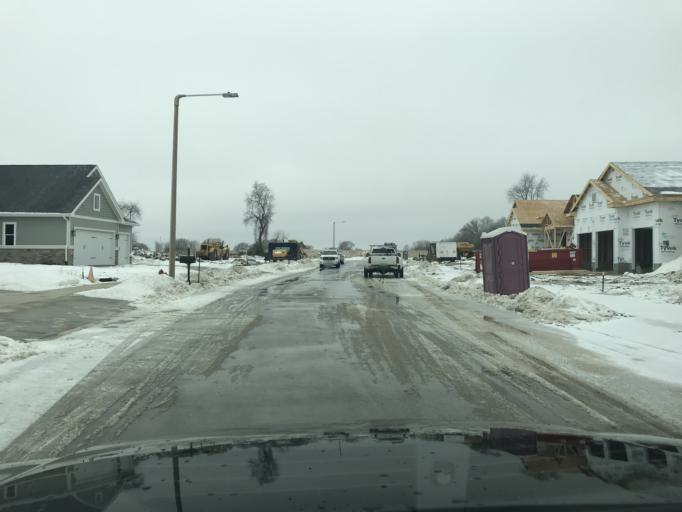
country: US
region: Wisconsin
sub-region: Dane County
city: Cottage Grove
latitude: 43.0966
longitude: -89.2230
